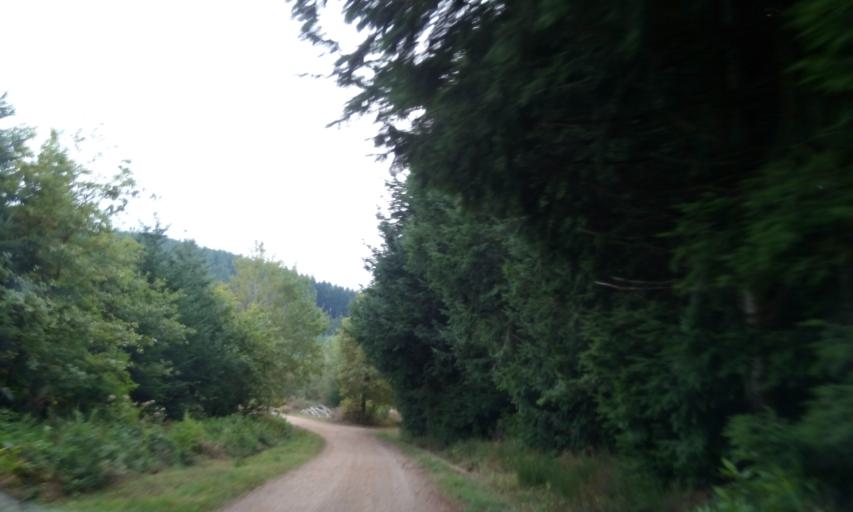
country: FR
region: Rhone-Alpes
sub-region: Departement du Rhone
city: Cublize
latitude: 46.0288
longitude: 4.4245
